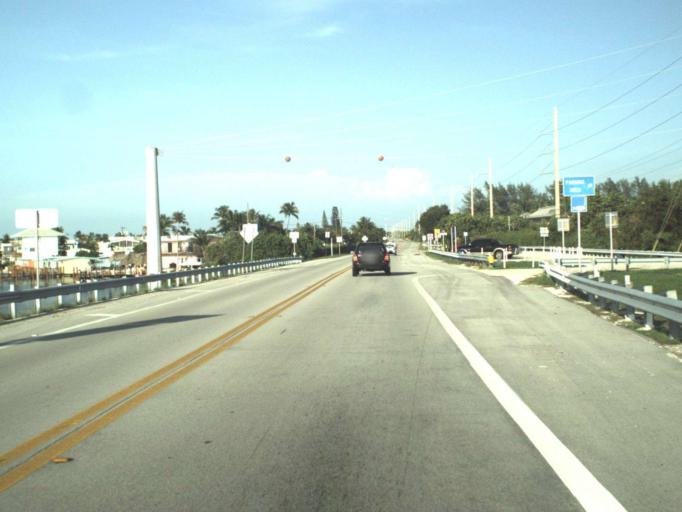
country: US
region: Florida
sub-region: Monroe County
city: Islamorada
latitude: 24.8033
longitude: -80.8503
